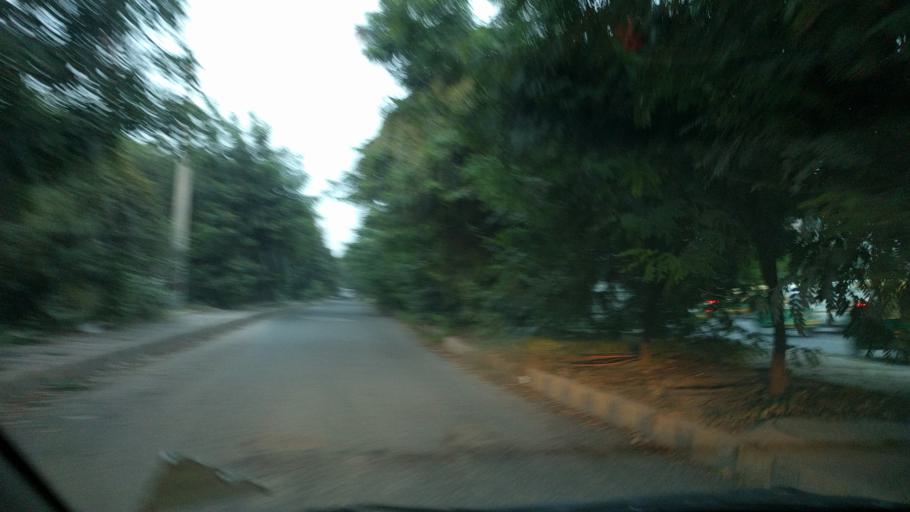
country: IN
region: Haryana
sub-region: Gurgaon
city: Gurgaon
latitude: 28.4520
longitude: 77.0657
